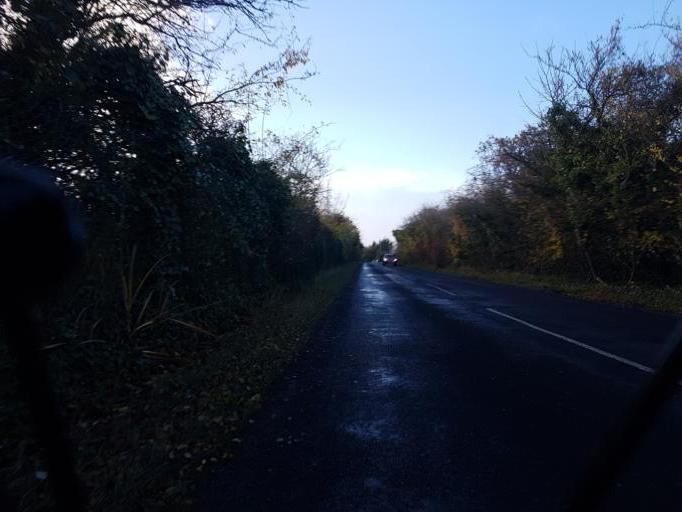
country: GB
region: England
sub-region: Kent
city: Sittingbourne
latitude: 51.3234
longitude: 0.7327
